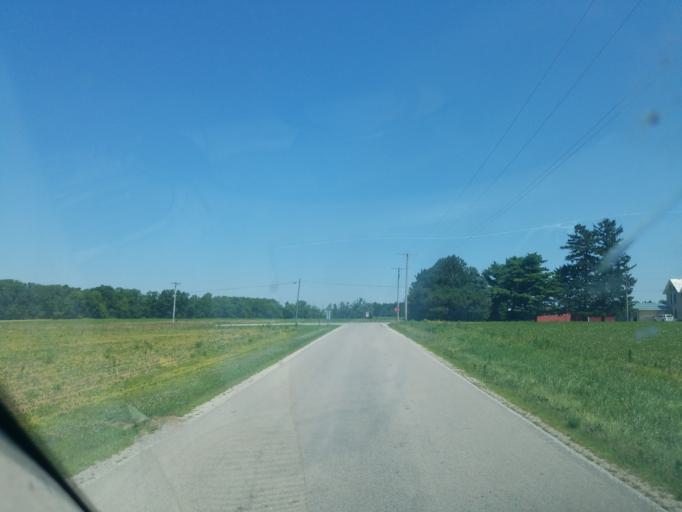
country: US
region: Ohio
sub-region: Mercer County
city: Rockford
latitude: 40.7417
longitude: -84.7370
